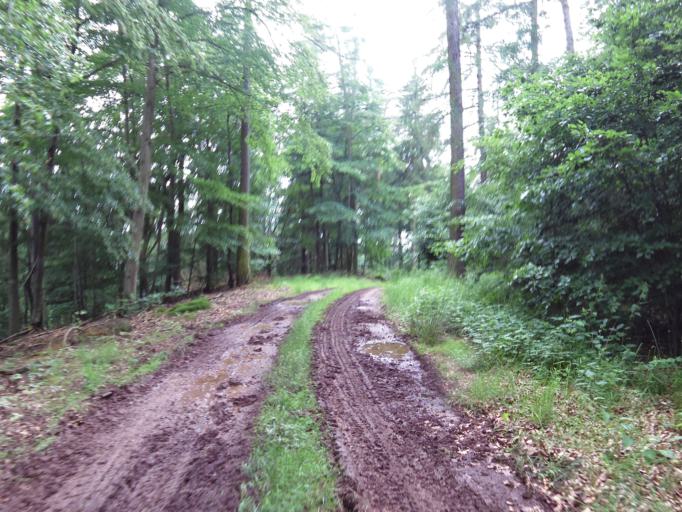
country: DE
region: Thuringia
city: Wolfsburg-Unkeroda
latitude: 50.9249
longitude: 10.2977
